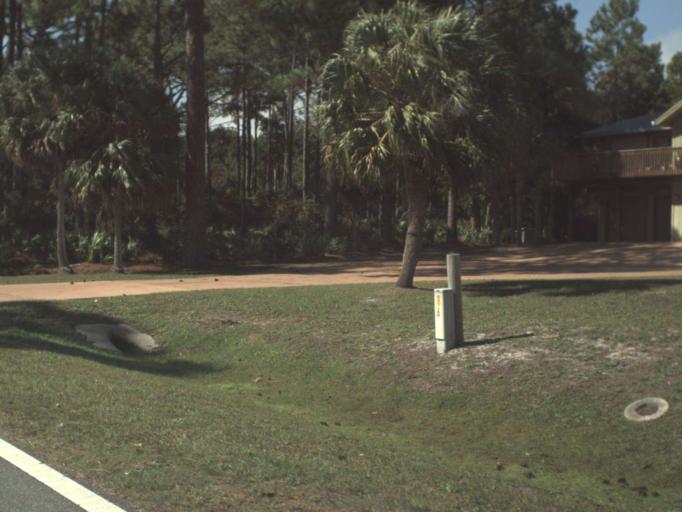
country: US
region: Florida
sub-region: Franklin County
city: Carrabelle
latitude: 29.9061
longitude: -84.5444
